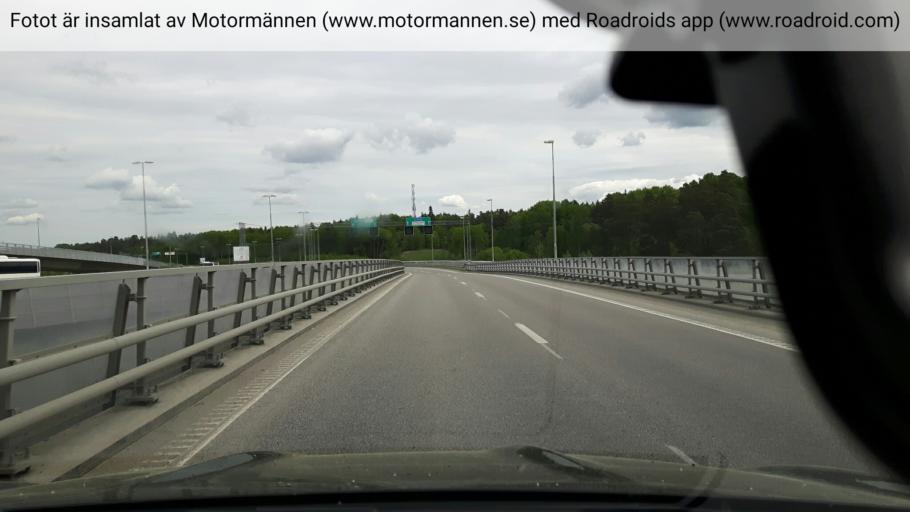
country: SE
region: Stockholm
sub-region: Stockholms Kommun
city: Kista
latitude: 59.3885
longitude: 17.9434
